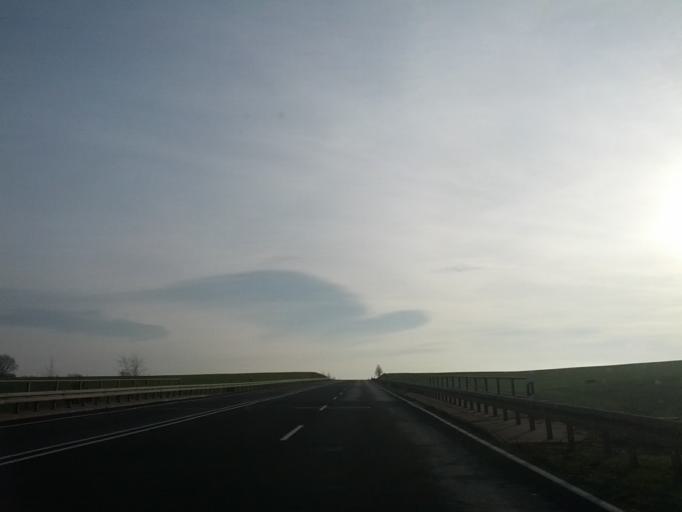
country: DE
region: Thuringia
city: Barchfeld
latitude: 50.8111
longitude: 10.3068
